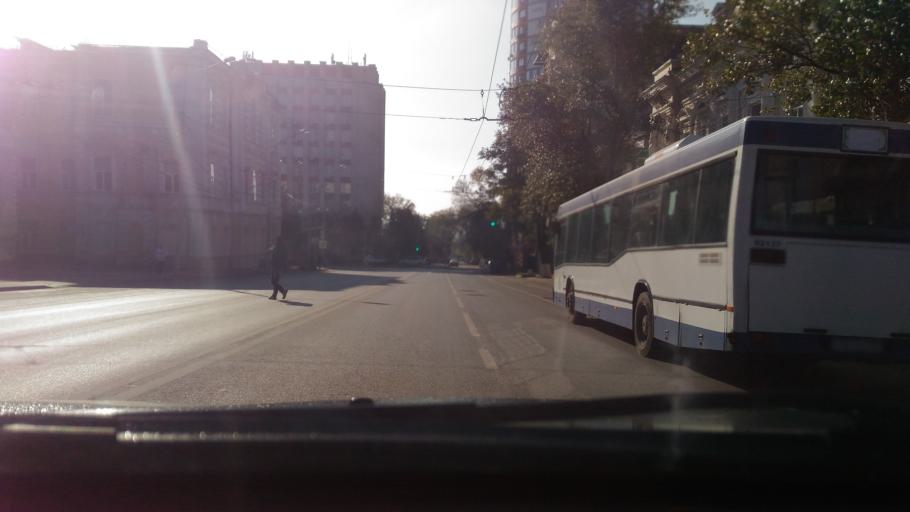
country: RU
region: Rostov
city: Rostov-na-Donu
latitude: 47.2301
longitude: 39.7624
